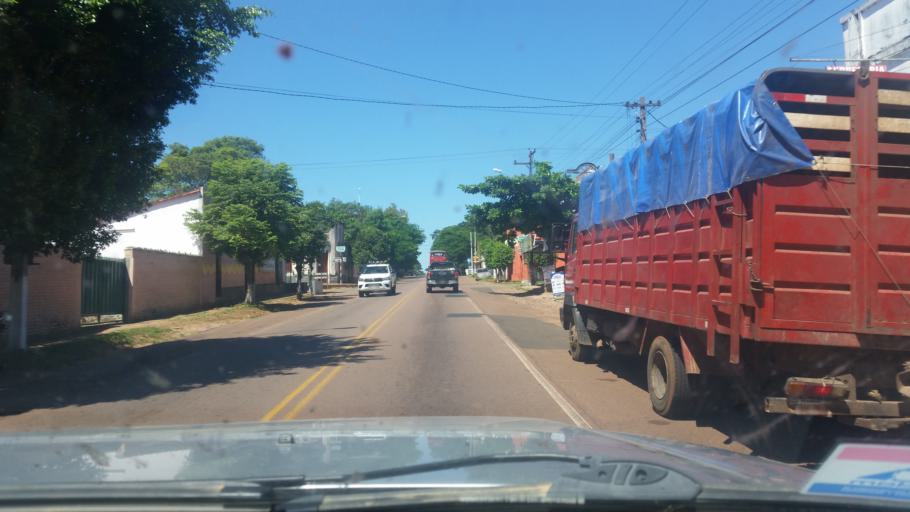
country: PY
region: Paraguari
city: Quiindy
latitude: -25.8793
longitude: -57.2898
